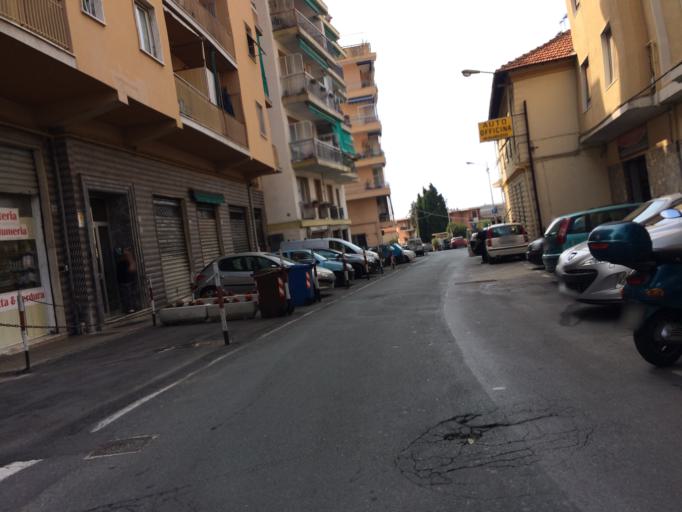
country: IT
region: Liguria
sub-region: Provincia di Imperia
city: San Remo
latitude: 43.8266
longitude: 7.7730
